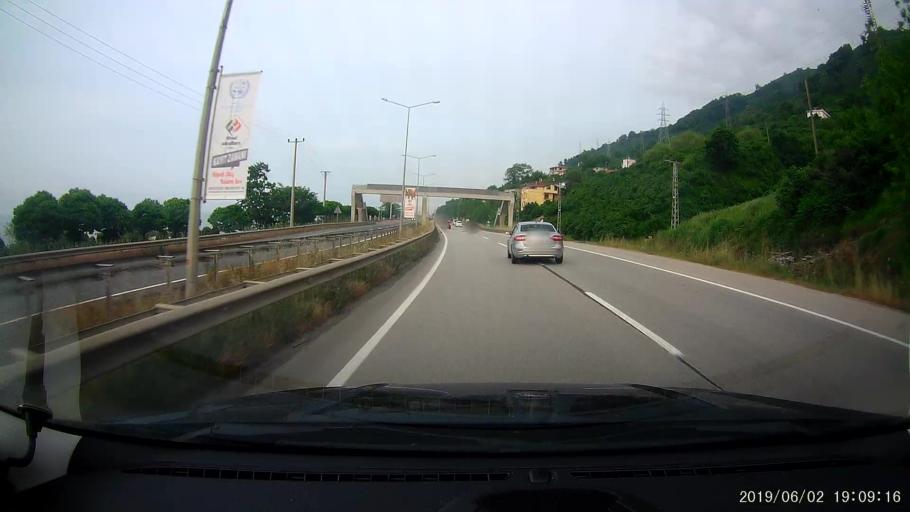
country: TR
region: Ordu
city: Gulyali
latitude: 40.9734
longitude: 38.0247
